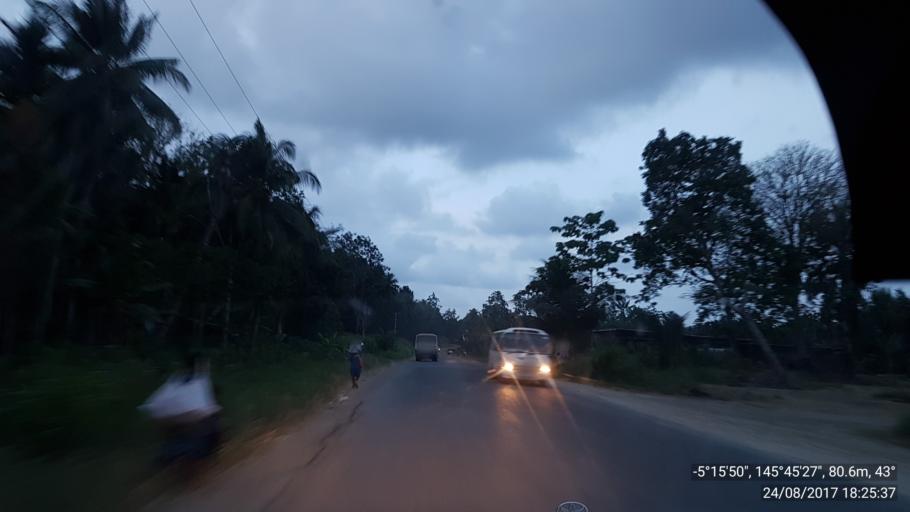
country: PG
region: Madang
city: Madang
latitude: -5.2642
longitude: 145.7575
